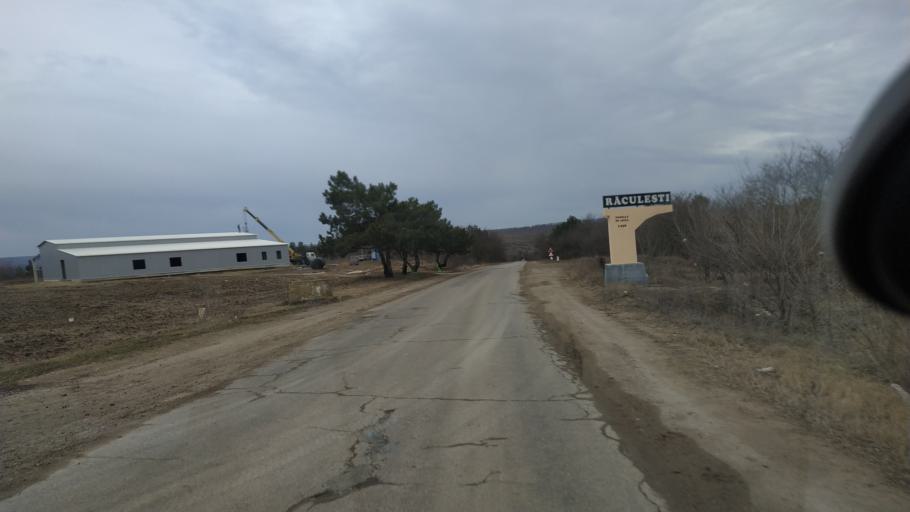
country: MD
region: Telenesti
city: Cocieri
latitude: 47.2671
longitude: 29.0820
